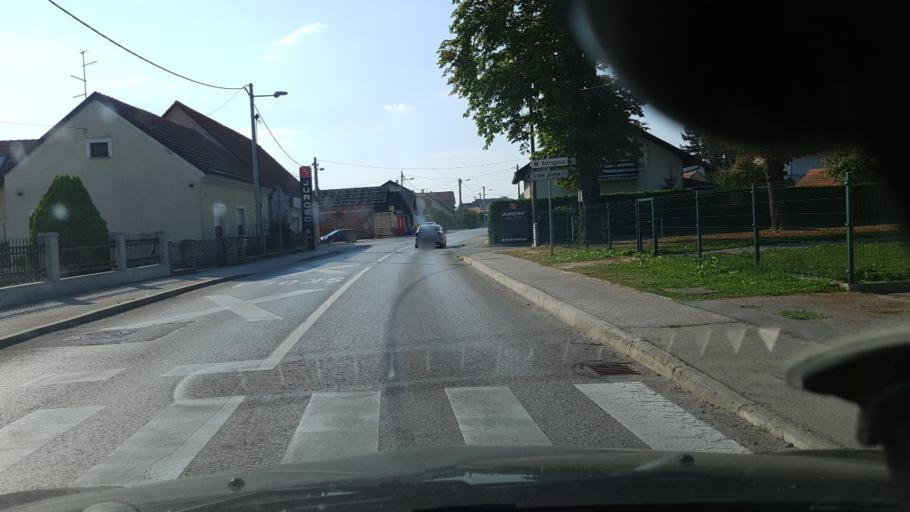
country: HR
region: Zagrebacka
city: Brdovec
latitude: 45.8652
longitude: 15.7678
